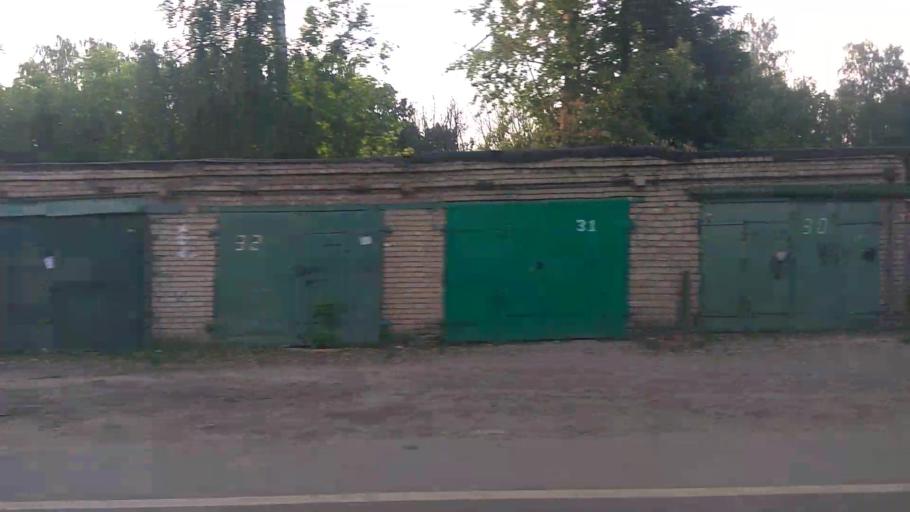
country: RU
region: Moskovskaya
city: Korolev
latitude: 55.9246
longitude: 37.7873
